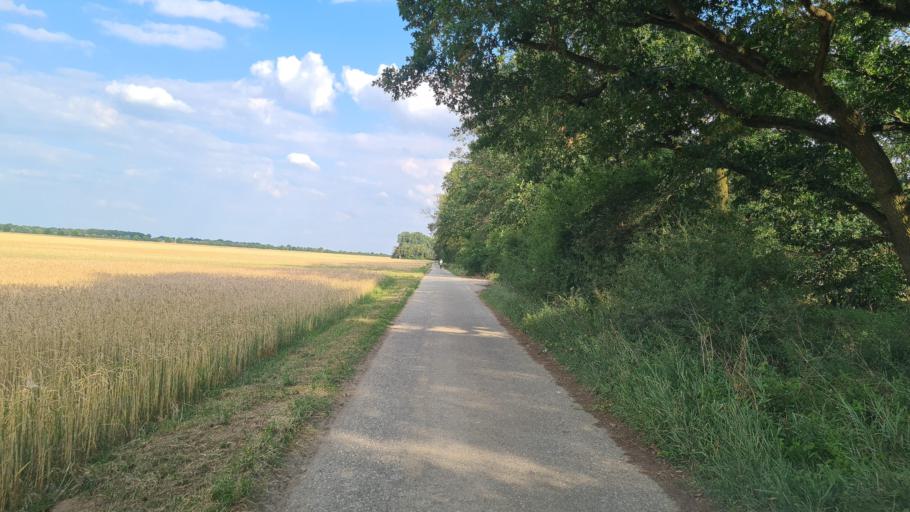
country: DE
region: Saxony-Anhalt
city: Pretzsch
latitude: 51.7631
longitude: 12.8458
